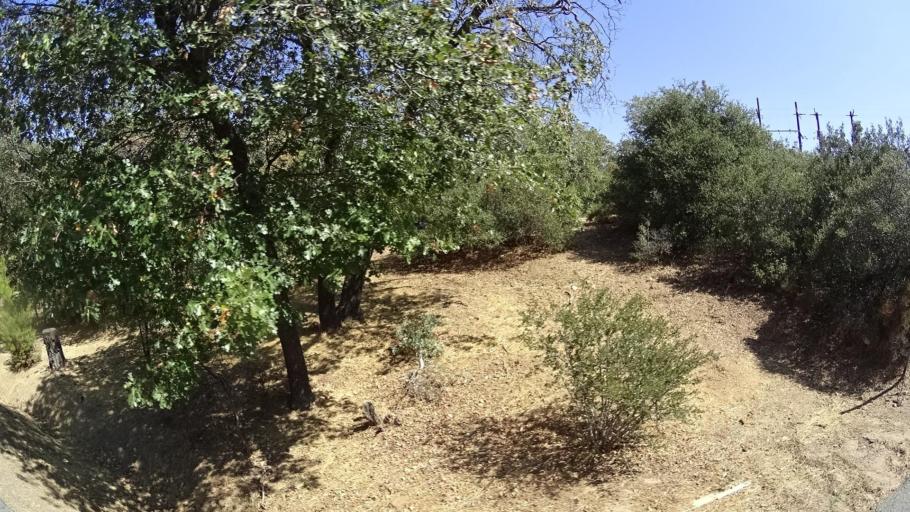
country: US
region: California
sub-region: San Diego County
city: Julian
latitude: 33.0741
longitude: -116.5838
